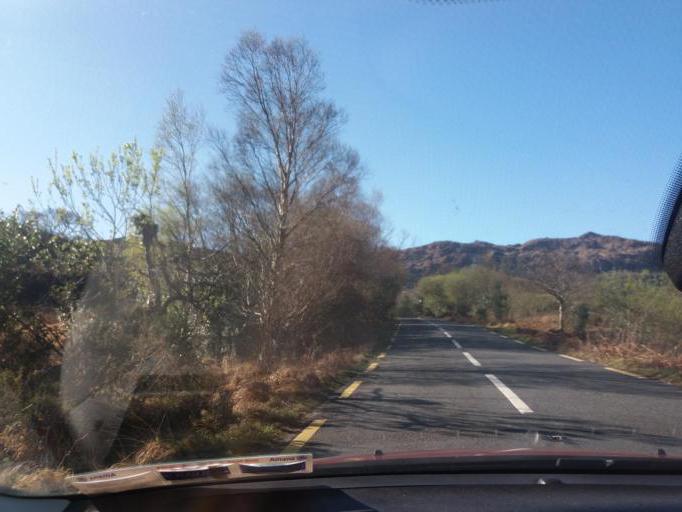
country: IE
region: Munster
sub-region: Ciarrai
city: Cill Airne
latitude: 51.9949
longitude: -9.5512
